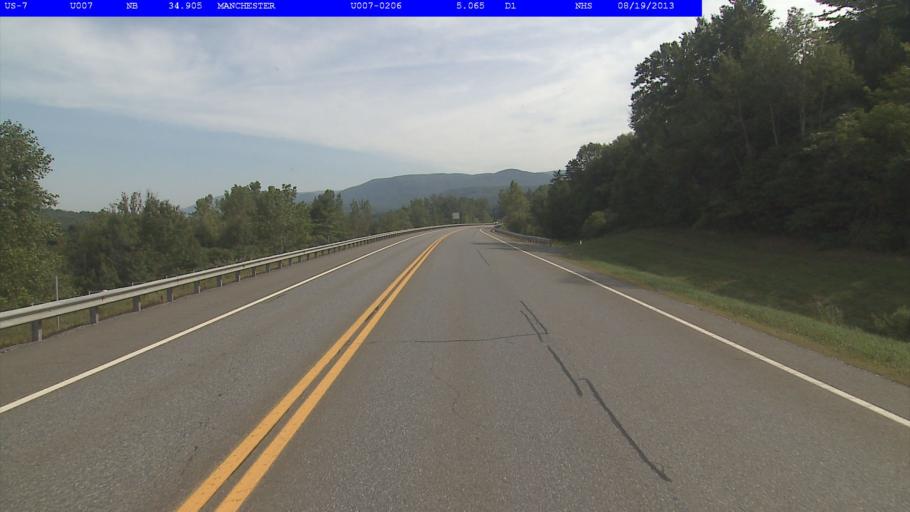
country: US
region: Vermont
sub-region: Bennington County
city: Manchester Center
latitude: 43.1783
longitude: -73.0264
